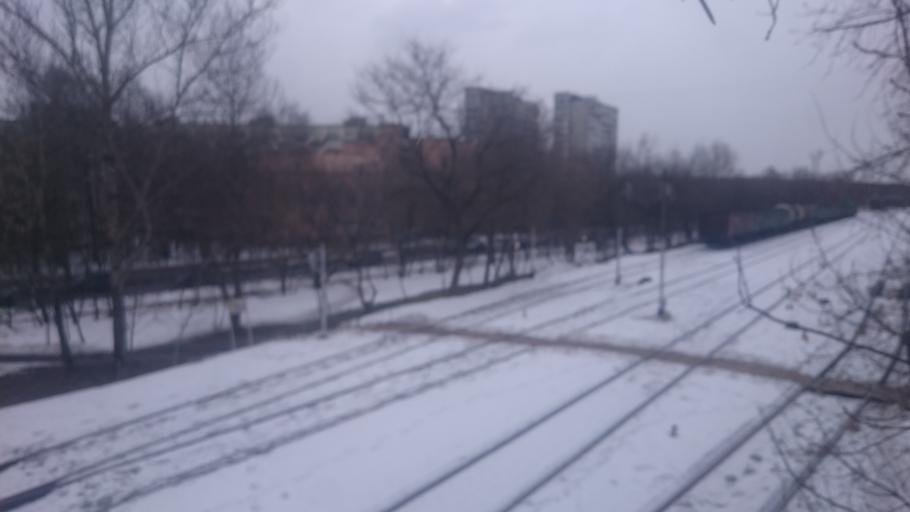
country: RU
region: Moscow
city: Biryulevo
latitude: 55.5897
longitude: 37.6680
